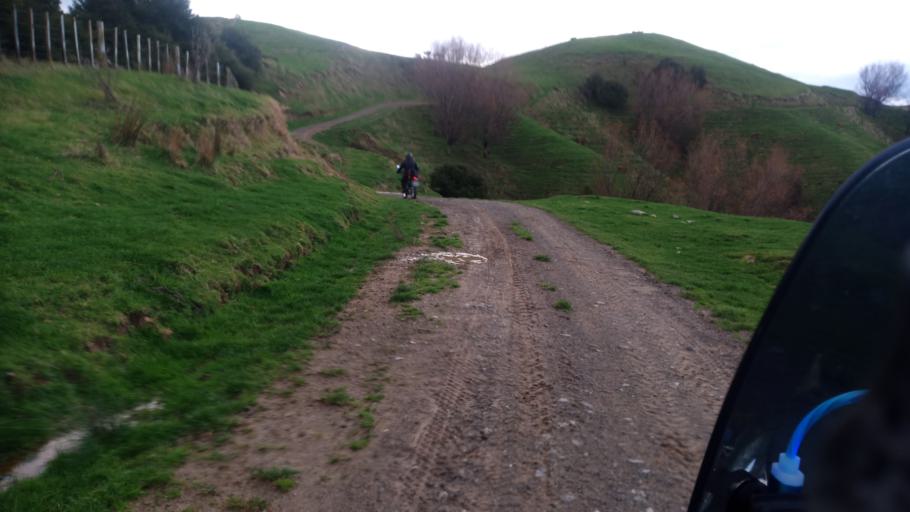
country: NZ
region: Gisborne
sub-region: Gisborne District
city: Gisborne
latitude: -38.3438
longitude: 177.9153
